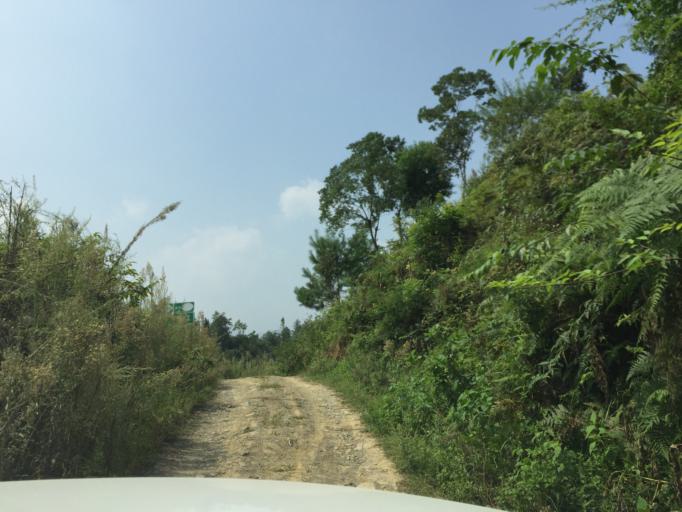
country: CN
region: Guizhou Sheng
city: Qinglong
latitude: 28.2938
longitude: 108.1101
